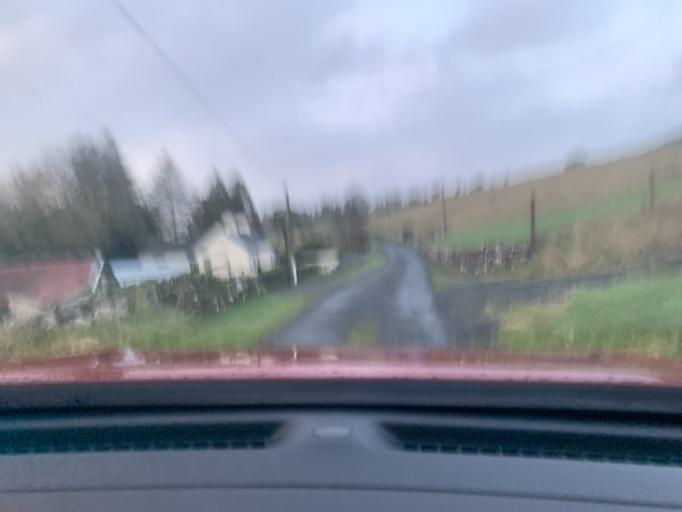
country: IE
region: Connaught
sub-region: Sligo
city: Ballymote
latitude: 54.0542
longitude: -8.3964
